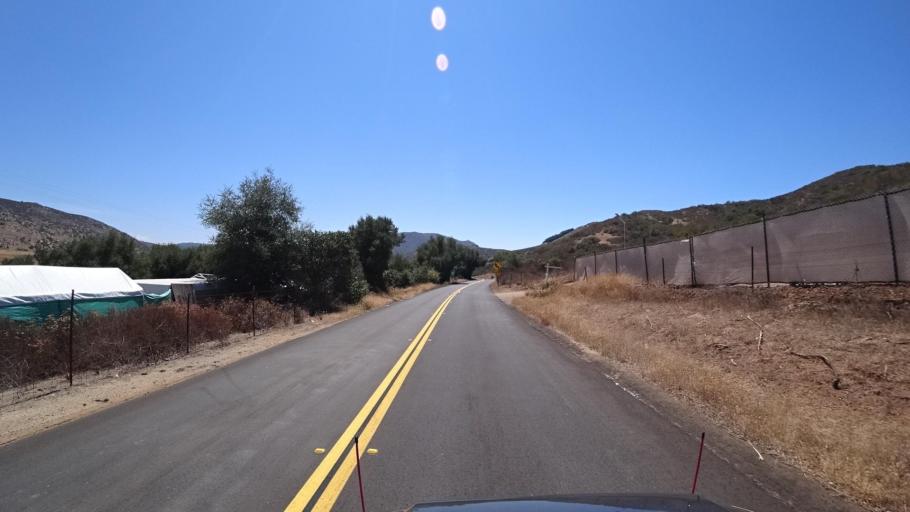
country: US
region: California
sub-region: San Diego County
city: Rainbow
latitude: 33.3569
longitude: -117.1360
